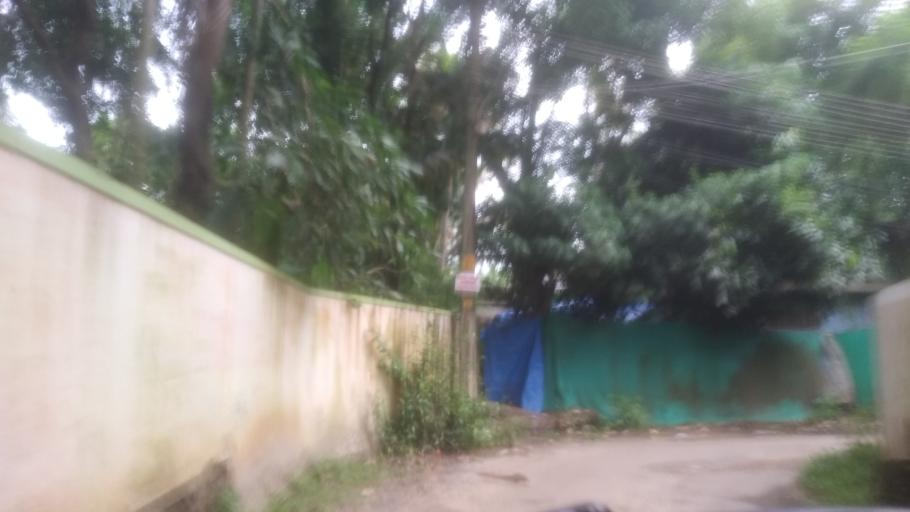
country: IN
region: Kerala
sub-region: Ernakulam
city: Elur
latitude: 10.0954
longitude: 76.2103
